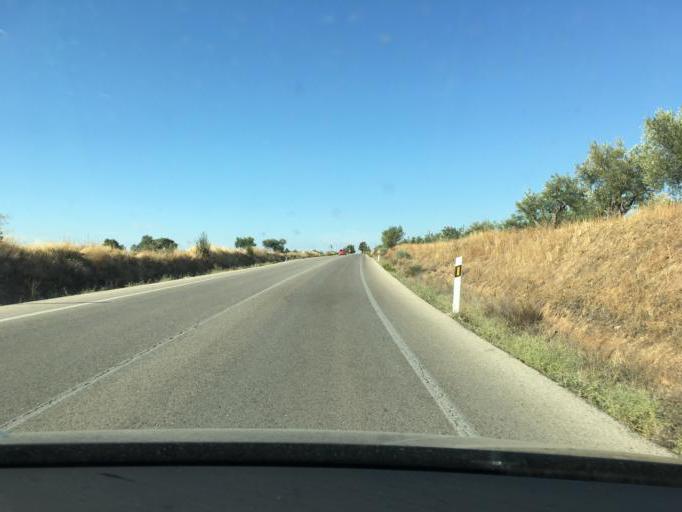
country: ES
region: Madrid
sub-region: Provincia de Madrid
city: Torremocha de Jarama
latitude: 40.8384
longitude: -3.5129
